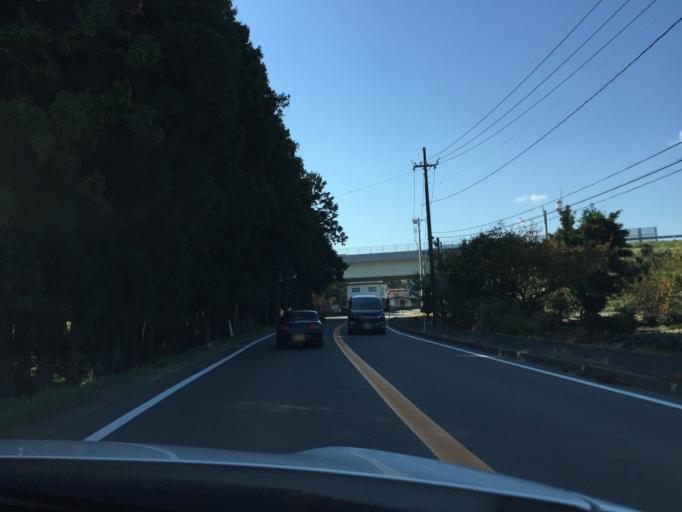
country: JP
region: Miyagi
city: Marumori
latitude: 37.7794
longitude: 140.8979
